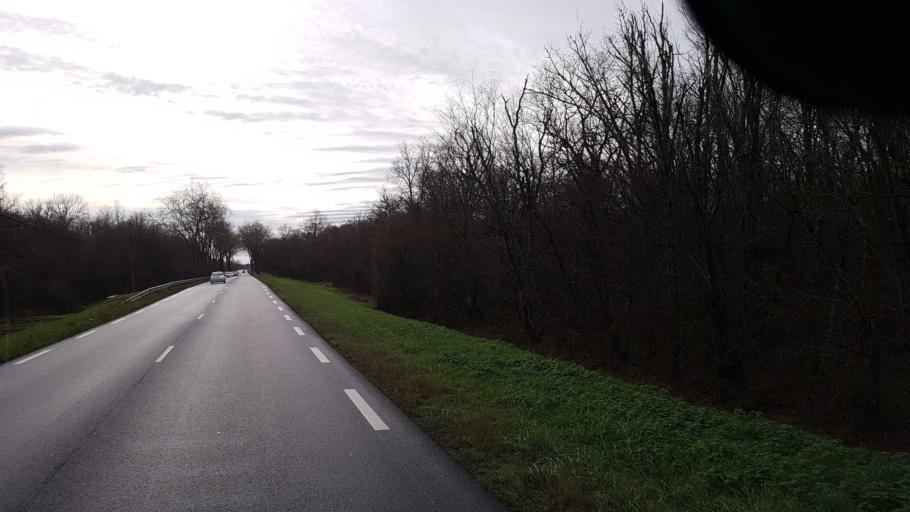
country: FR
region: Centre
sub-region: Departement du Loiret
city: Saint-Cyr-en-Val
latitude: 47.7801
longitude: 1.9355
